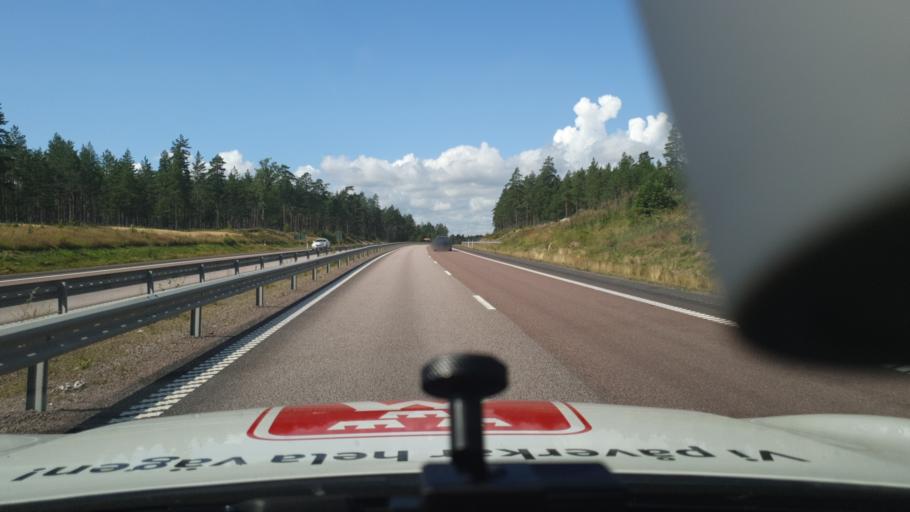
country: SE
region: Vaermland
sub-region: Kils Kommun
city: Kil
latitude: 59.3845
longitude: 13.3337
